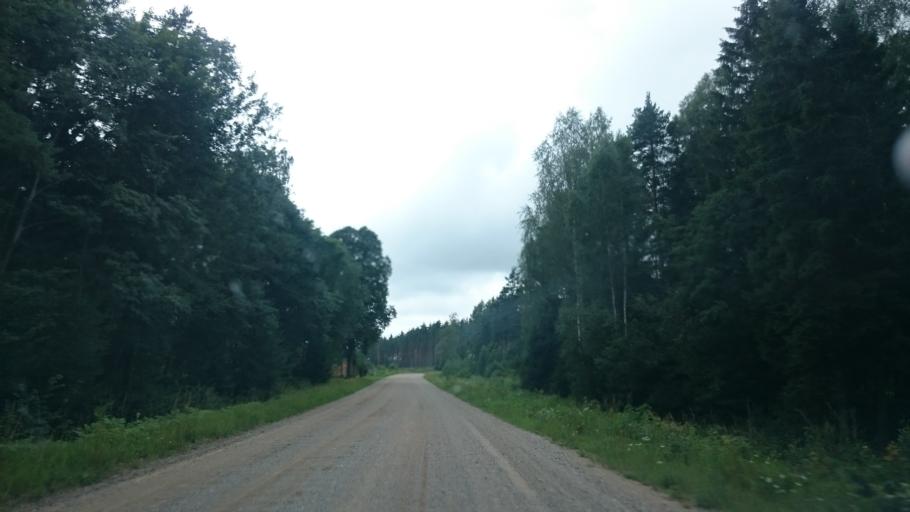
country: LV
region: Pavilostas
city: Pavilosta
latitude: 56.8574
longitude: 21.2325
